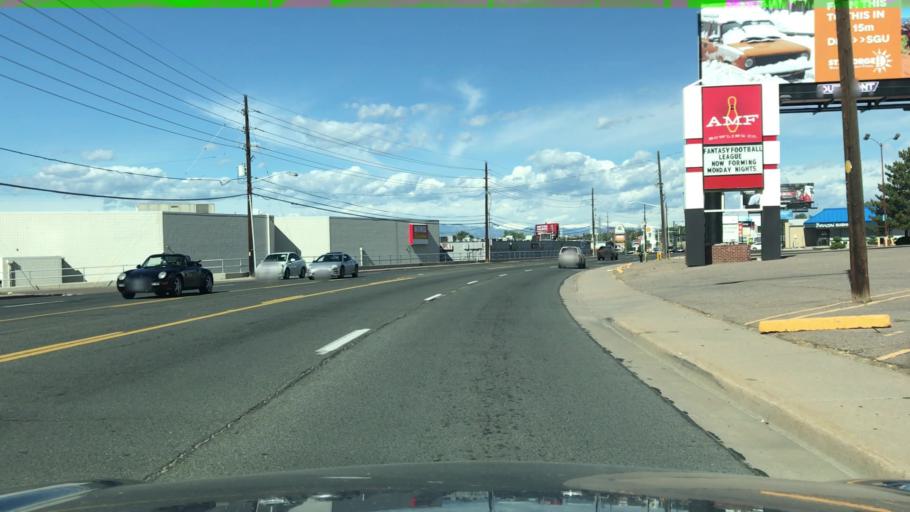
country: US
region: Colorado
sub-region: Arapahoe County
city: Glendale
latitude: 39.7009
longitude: -104.9100
